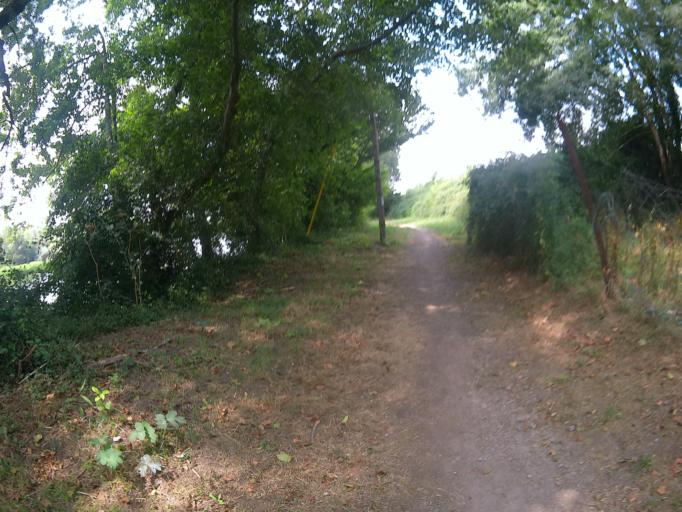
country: PT
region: Viana do Castelo
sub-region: Ponte de Lima
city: Ponte de Lima
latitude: 41.7783
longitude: -8.5805
